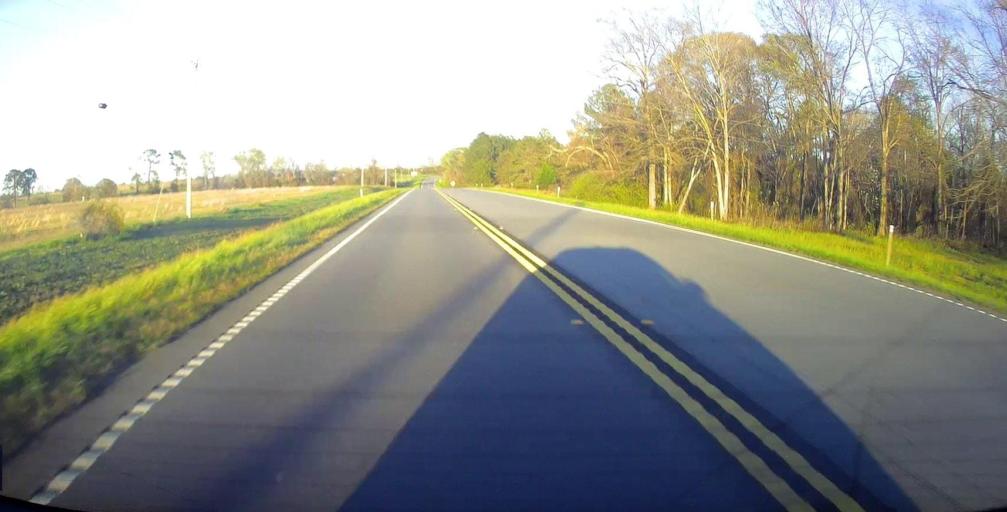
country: US
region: Georgia
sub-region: Crisp County
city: Cordele
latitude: 31.9554
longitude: -83.6844
